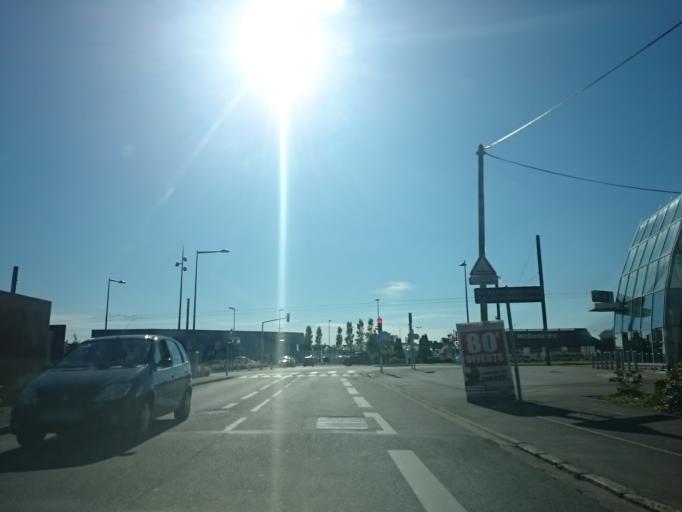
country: FR
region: Brittany
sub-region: Departement du Finistere
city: Brest
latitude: 48.4182
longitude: -4.4671
